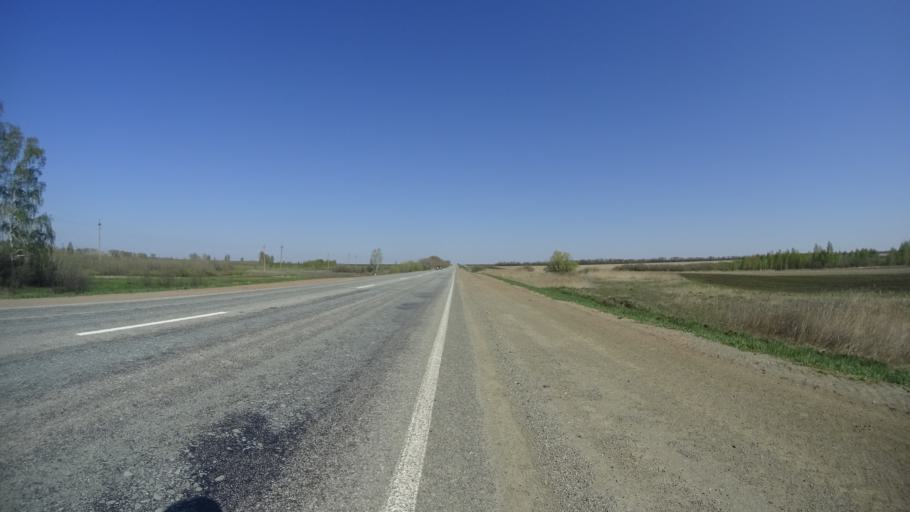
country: RU
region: Chelyabinsk
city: Troitsk
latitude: 54.2015
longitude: 61.4320
